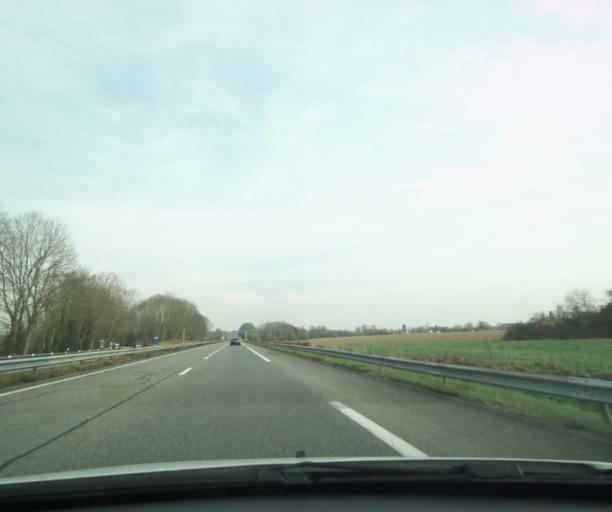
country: FR
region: Aquitaine
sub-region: Departement des Pyrenees-Atlantiques
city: Ousse
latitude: 43.3142
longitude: -0.2702
